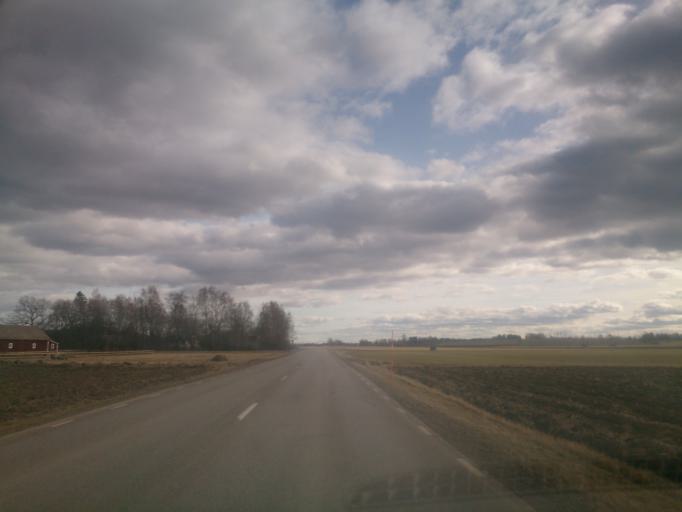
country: SE
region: OEstergoetland
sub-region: Motala Kommun
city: Borensberg
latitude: 58.4846
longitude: 15.2135
